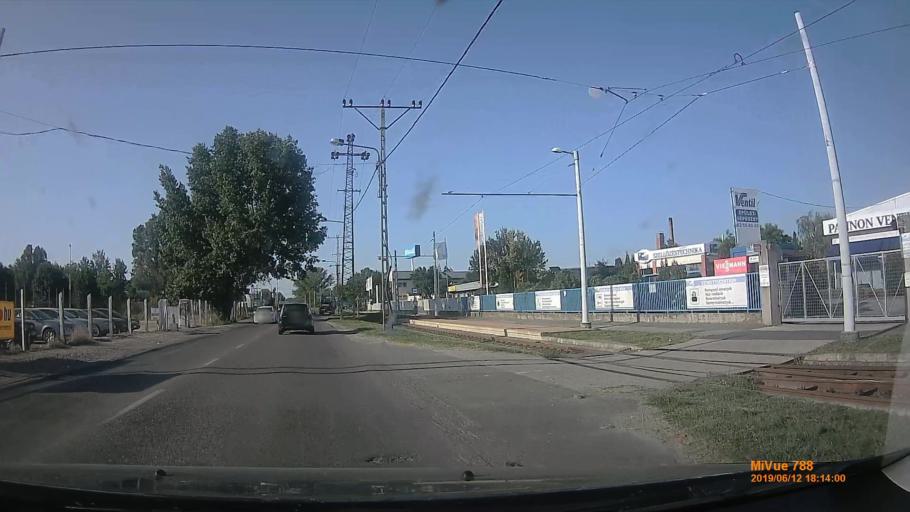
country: HU
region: Csongrad
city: Szeged
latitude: 46.2646
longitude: 20.1099
